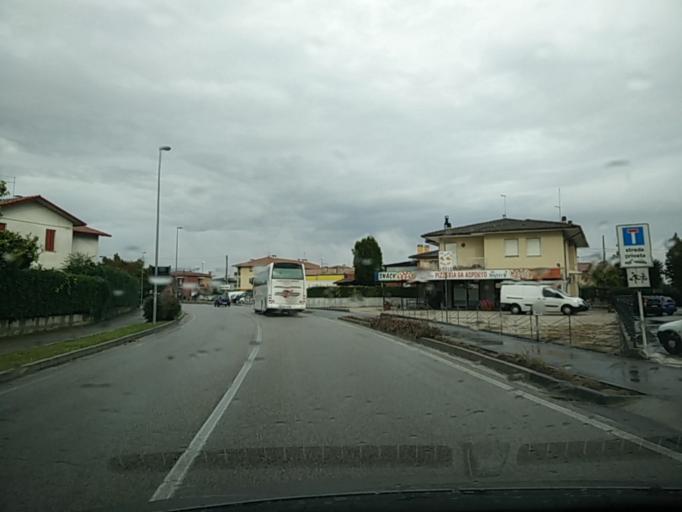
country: IT
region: Veneto
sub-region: Provincia di Vicenza
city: Rossano Veneto
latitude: 45.7068
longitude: 11.8071
